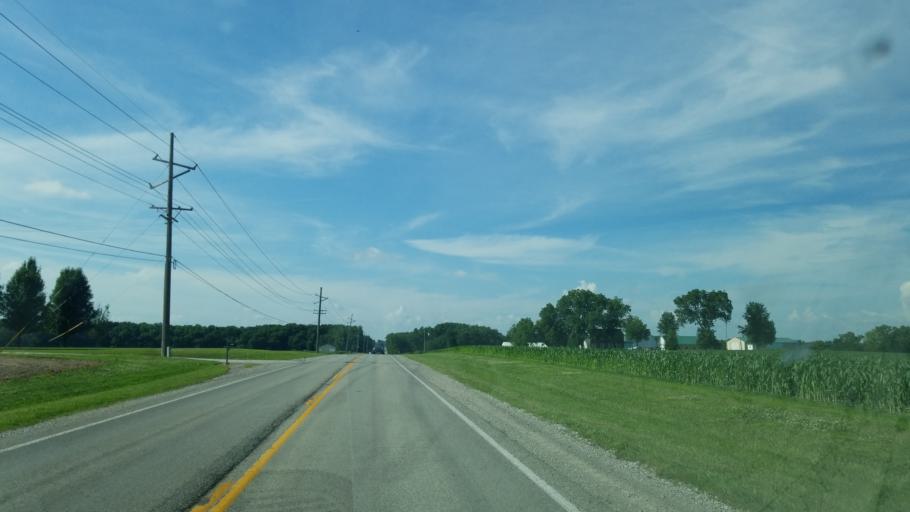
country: US
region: Illinois
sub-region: Saint Clair County
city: Lebanon
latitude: 38.5692
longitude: -89.8078
